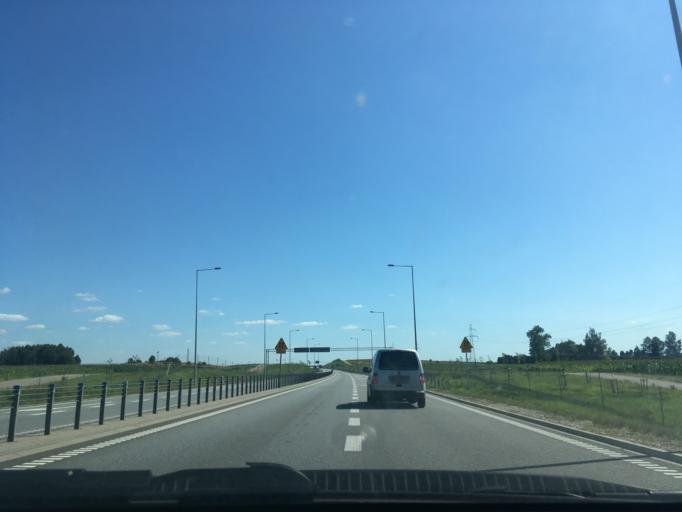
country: PL
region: Podlasie
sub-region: Powiat suwalski
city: Raczki
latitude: 53.9116
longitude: 22.8379
